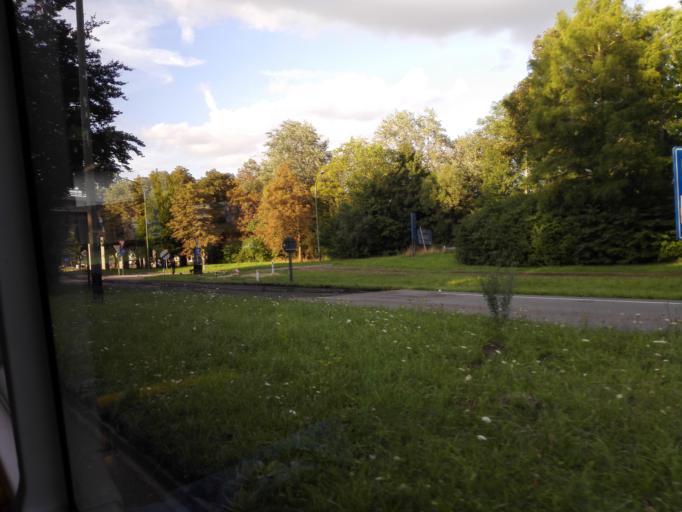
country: BE
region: Flanders
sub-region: Provincie Vlaams-Brabant
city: Kraainem
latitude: 50.8643
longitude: 4.4515
